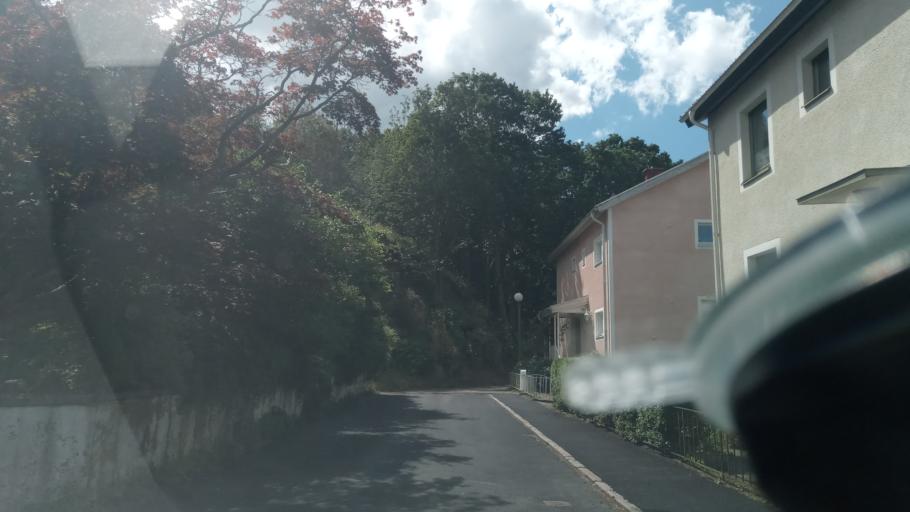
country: SE
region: Vaestra Goetaland
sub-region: Molndal
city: Moelndal
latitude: 57.6930
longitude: 12.0068
